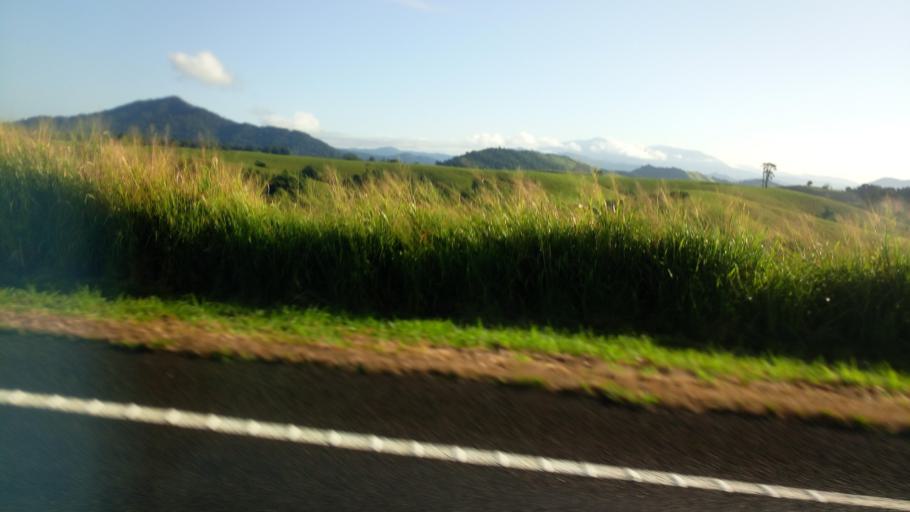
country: AU
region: Queensland
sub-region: Cassowary Coast
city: Innisfail
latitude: -17.6230
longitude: 145.8220
